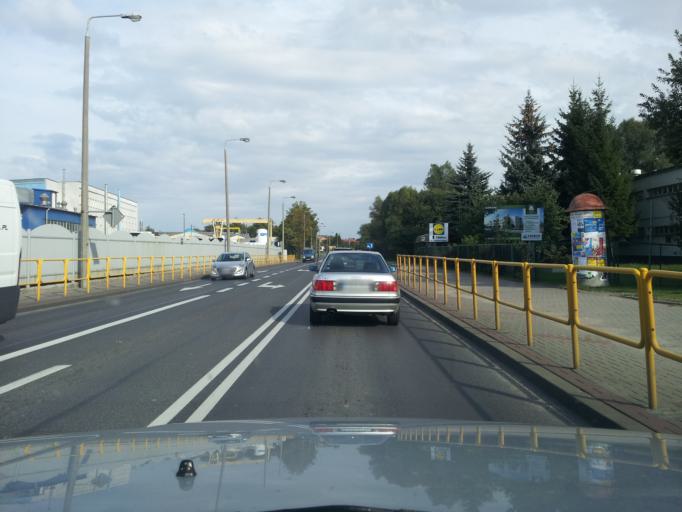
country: PL
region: Warmian-Masurian Voivodeship
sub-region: Powiat ostrodzki
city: Ostroda
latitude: 53.6970
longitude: 19.9395
